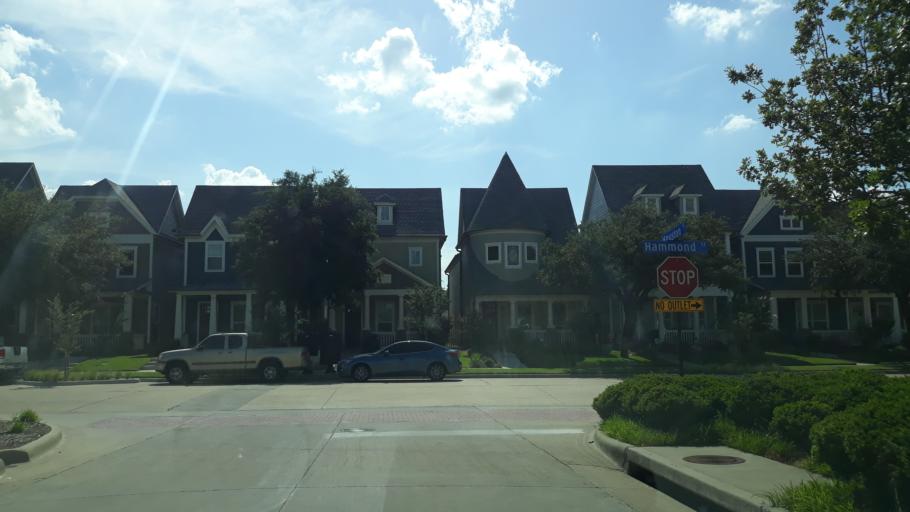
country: US
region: Texas
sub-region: Dallas County
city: Coppell
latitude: 32.9534
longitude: -97.0064
